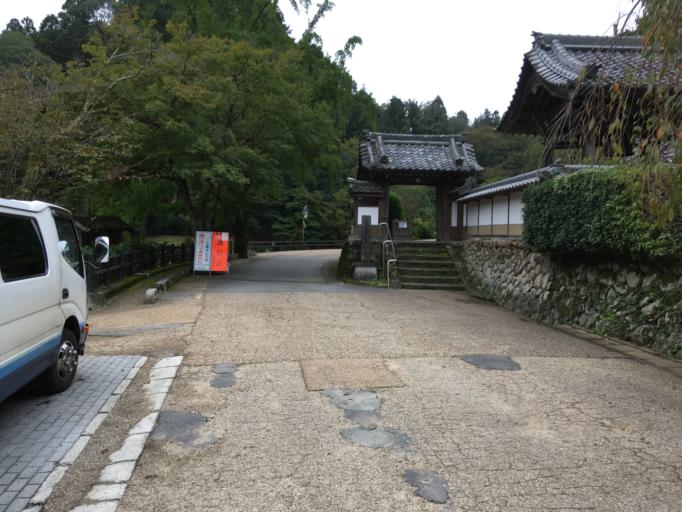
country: JP
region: Nara
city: Haibara-akanedai
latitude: 34.5629
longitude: 136.0159
